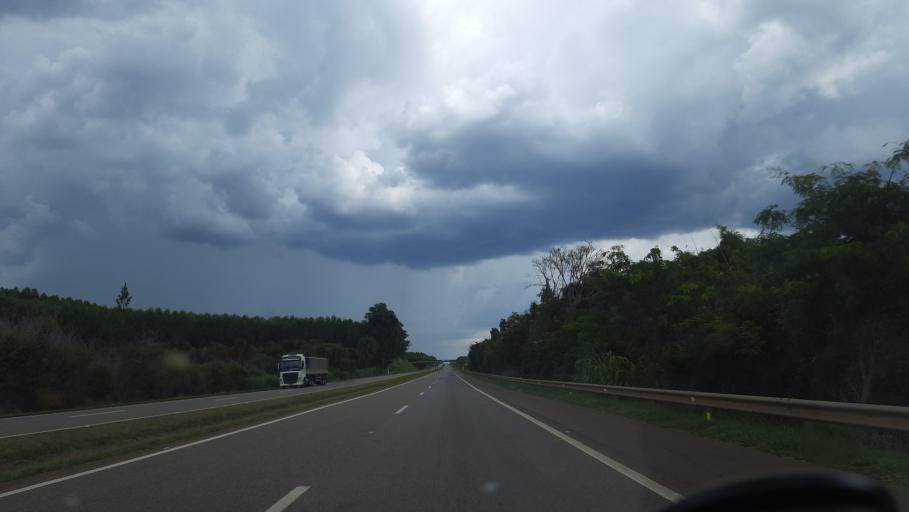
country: BR
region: Sao Paulo
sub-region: Casa Branca
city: Casa Branca
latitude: -21.8524
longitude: -47.0640
